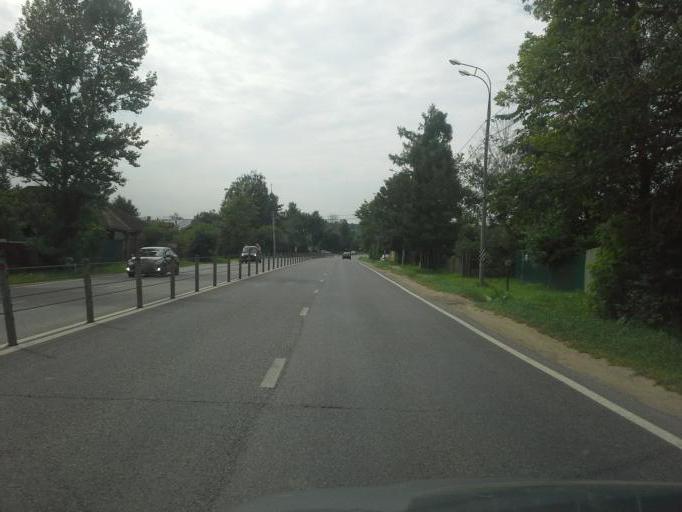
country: RU
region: Moskovskaya
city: Zhavoronki
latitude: 55.6549
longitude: 37.1396
